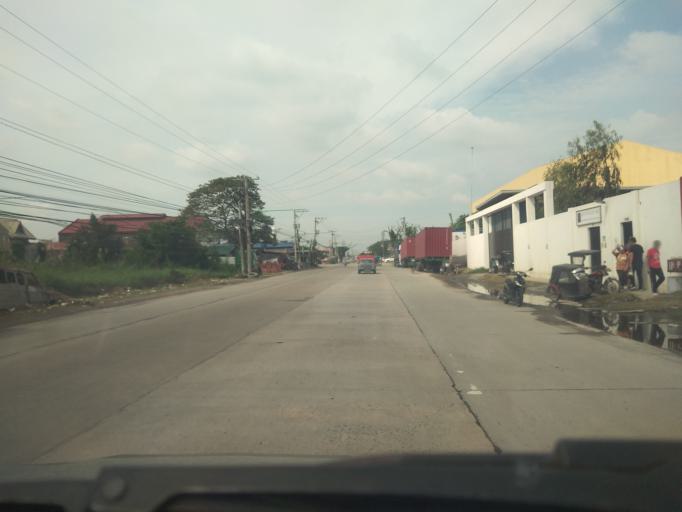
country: PH
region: Central Luzon
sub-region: Province of Pampanga
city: Santo Domingo
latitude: 15.0028
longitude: 120.7231
